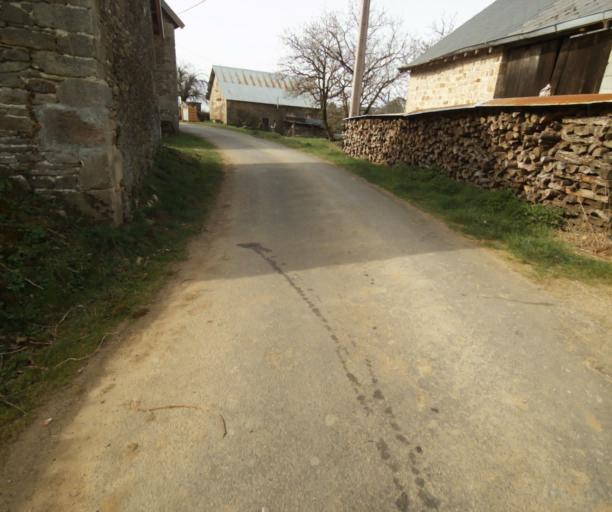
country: FR
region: Limousin
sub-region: Departement de la Correze
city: Correze
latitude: 45.4105
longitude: 1.8019
